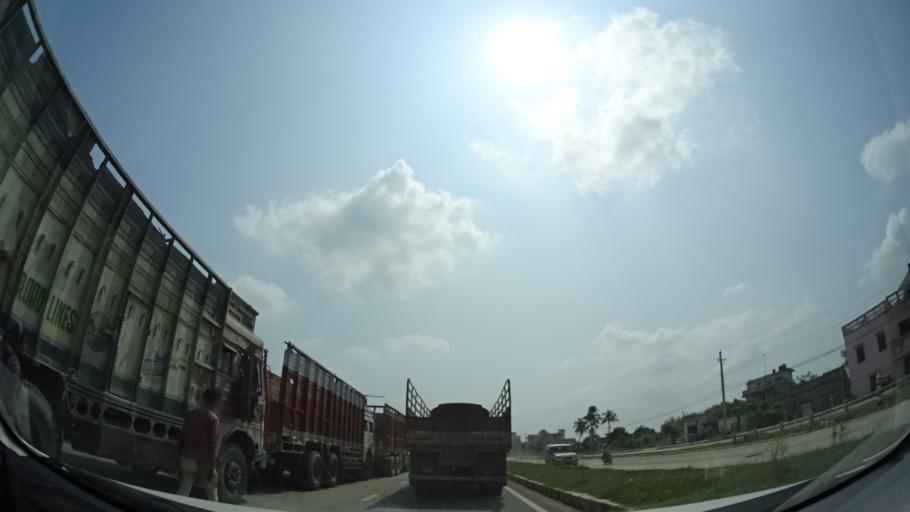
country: NP
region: Western Region
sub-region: Lumbini Zone
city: Bhairahawa
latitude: 27.4817
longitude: 83.4614
